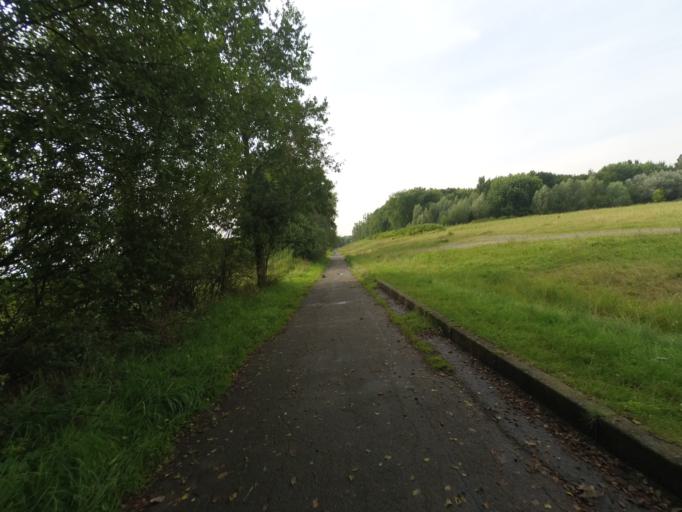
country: DE
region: Schleswig-Holstein
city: Oststeinbek
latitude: 53.5203
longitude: 10.1333
